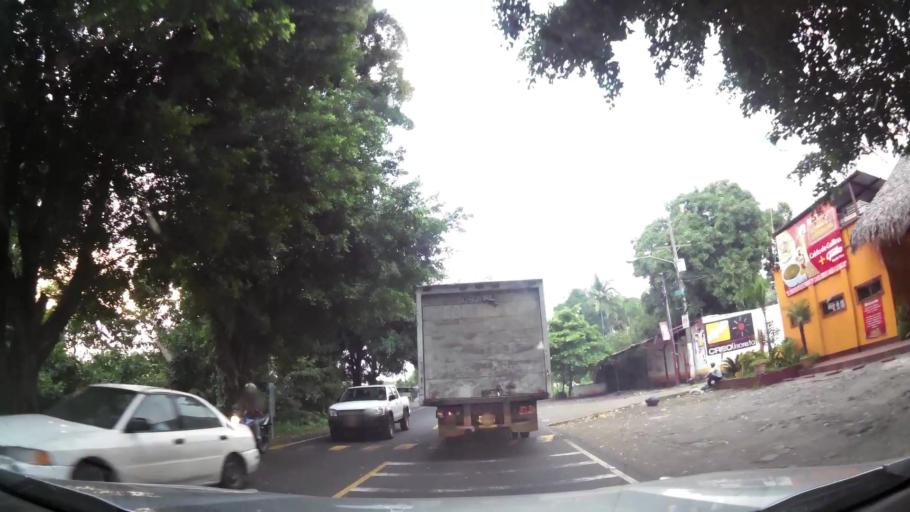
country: GT
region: Escuintla
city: Siquinala
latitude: 14.3019
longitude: -90.9565
